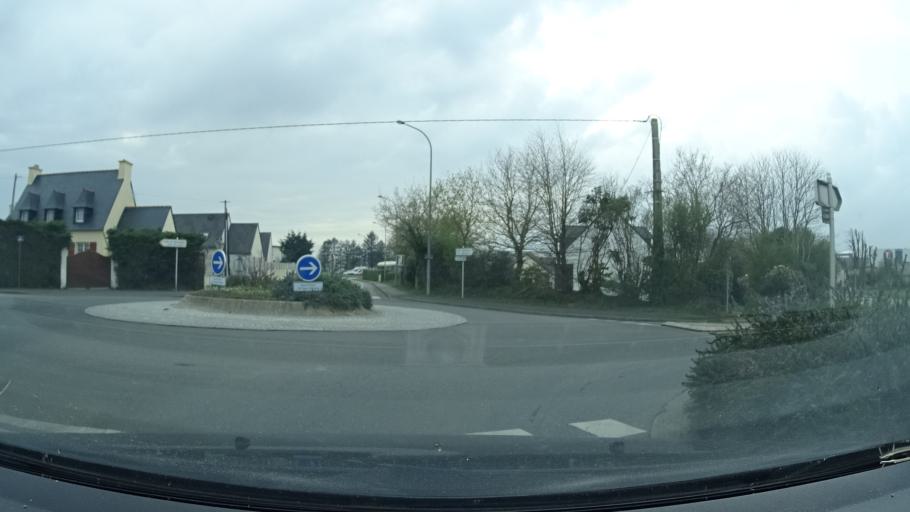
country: FR
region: Brittany
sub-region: Departement du Finistere
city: Guilers
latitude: 48.4270
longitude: -4.5672
